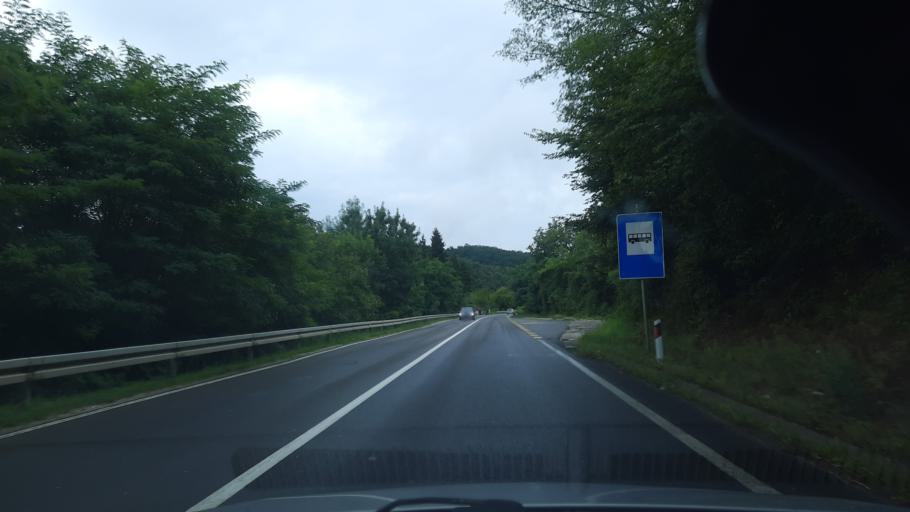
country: RS
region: Central Serbia
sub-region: Sumadijski Okrug
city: Knic
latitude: 43.9642
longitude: 20.8101
